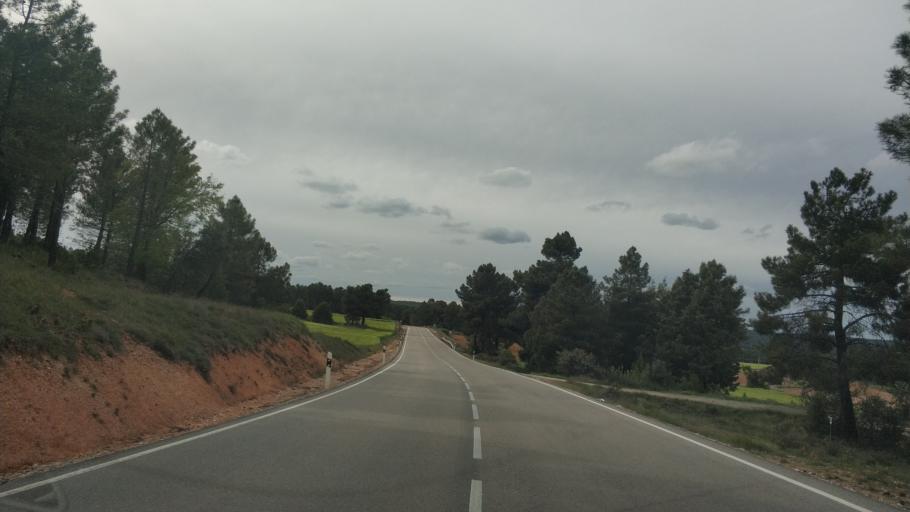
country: ES
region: Castille and Leon
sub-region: Provincia de Soria
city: Valdenebro
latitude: 41.5538
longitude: -2.9638
